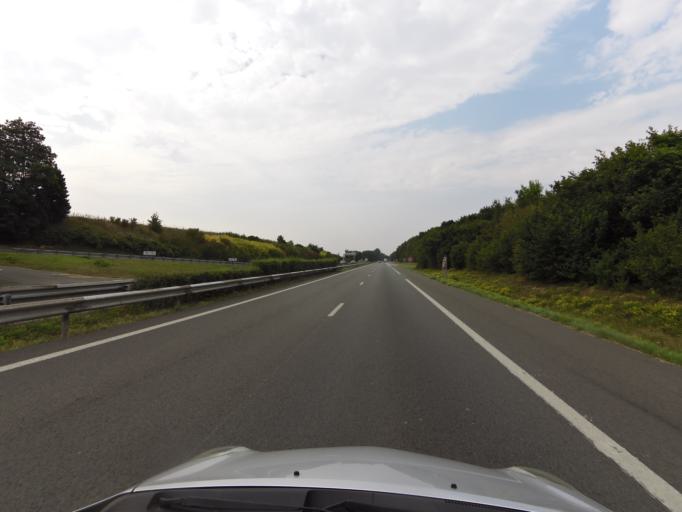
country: FR
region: Nord-Pas-de-Calais
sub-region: Departement du Pas-de-Calais
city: Bourlon
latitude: 50.1447
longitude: 3.1265
